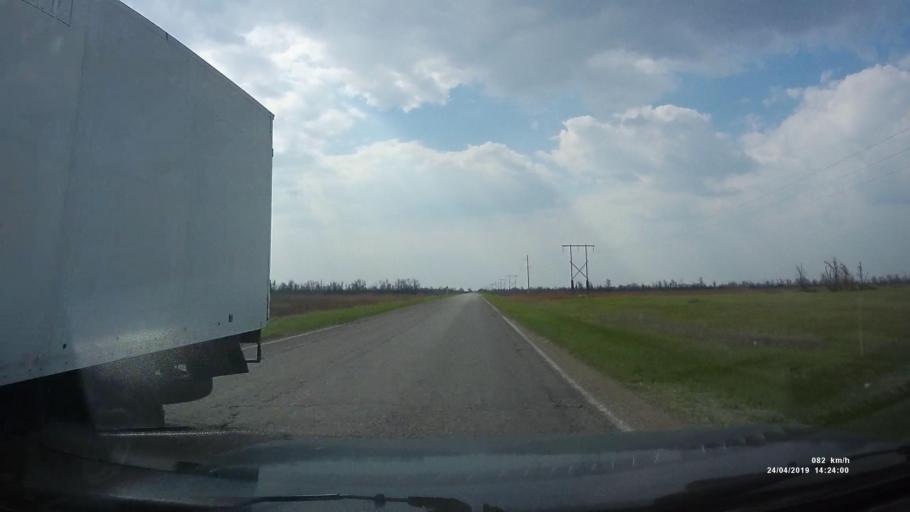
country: RU
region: Kalmykiya
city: Arshan'
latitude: 46.3269
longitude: 44.1059
